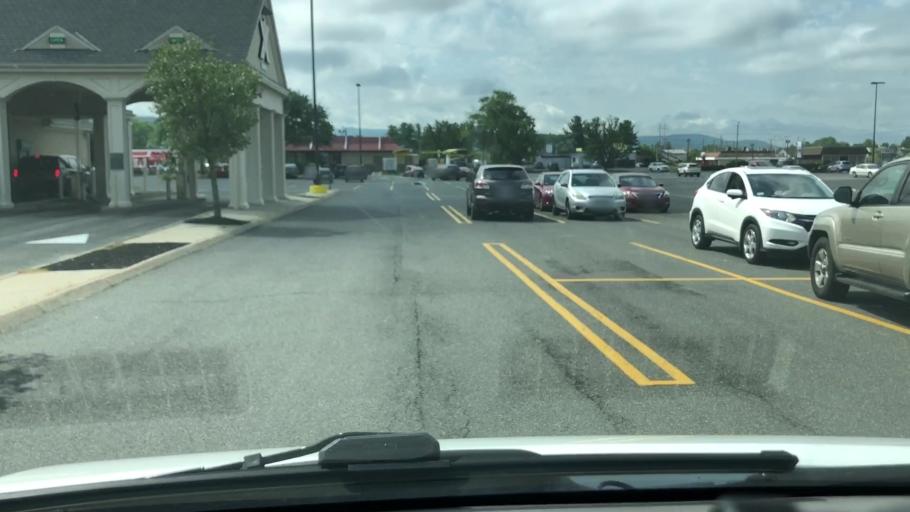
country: US
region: Massachusetts
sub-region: Berkshire County
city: Dalton
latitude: 42.4697
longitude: -73.2044
